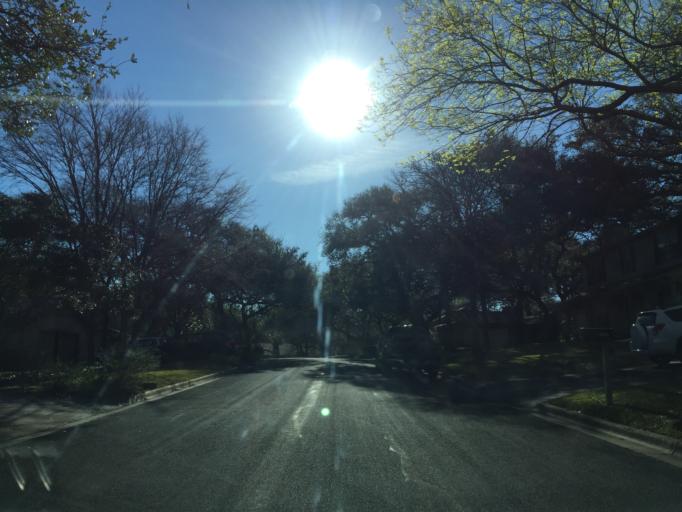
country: US
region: Texas
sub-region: Williamson County
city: Jollyville
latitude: 30.4071
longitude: -97.7384
